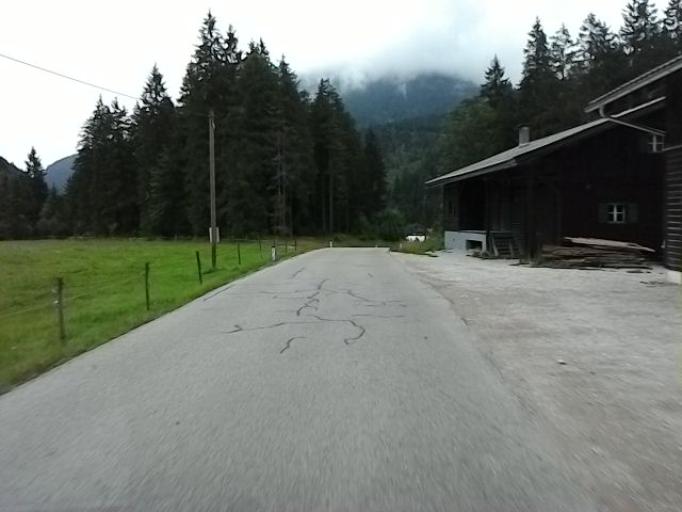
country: DE
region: Bavaria
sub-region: Upper Bavaria
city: Jachenau
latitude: 47.4800
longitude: 11.4630
